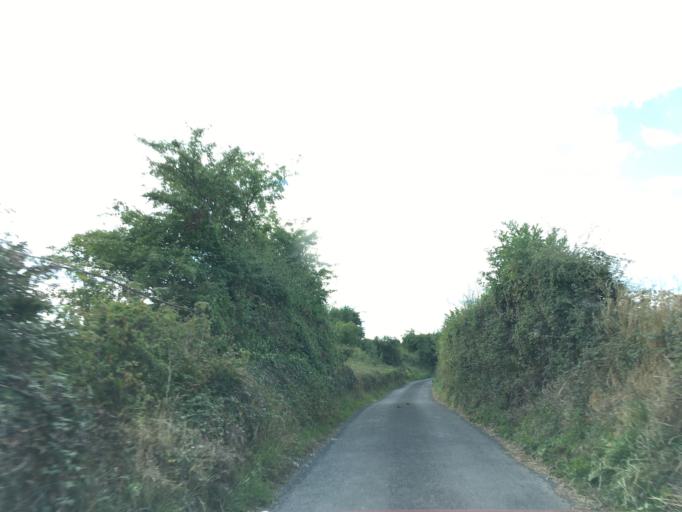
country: IE
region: Munster
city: Cashel
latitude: 52.5203
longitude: -7.8756
